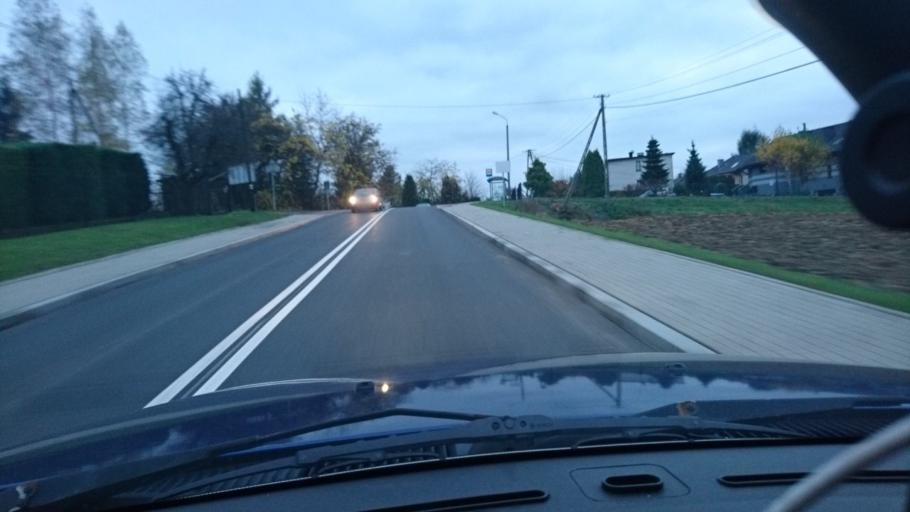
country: PL
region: Silesian Voivodeship
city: Janowice
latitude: 49.9037
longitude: 19.0827
